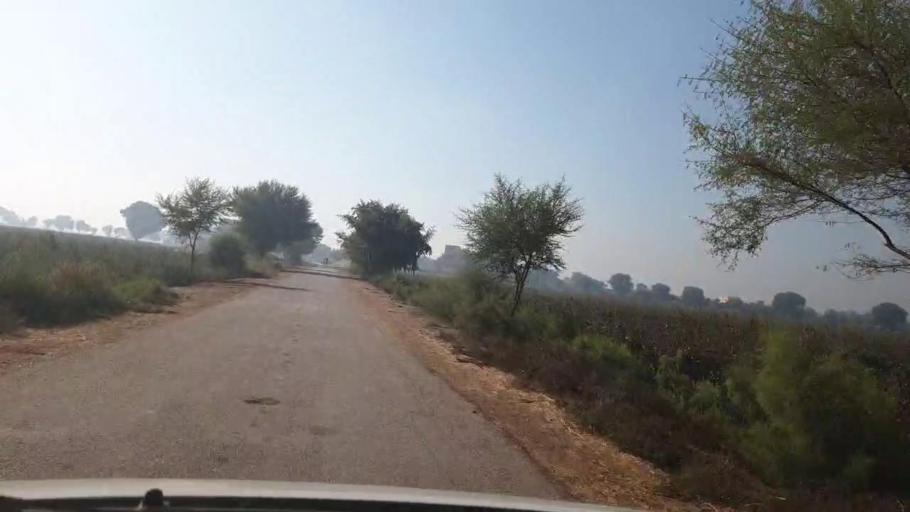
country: PK
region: Sindh
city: Dadu
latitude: 26.6524
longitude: 67.8223
